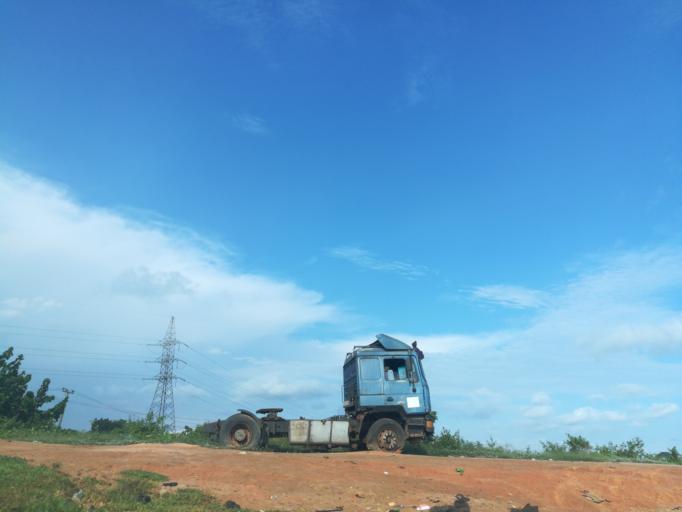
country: NG
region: Ogun
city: Ado Odo
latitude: 6.4978
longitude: 3.0858
